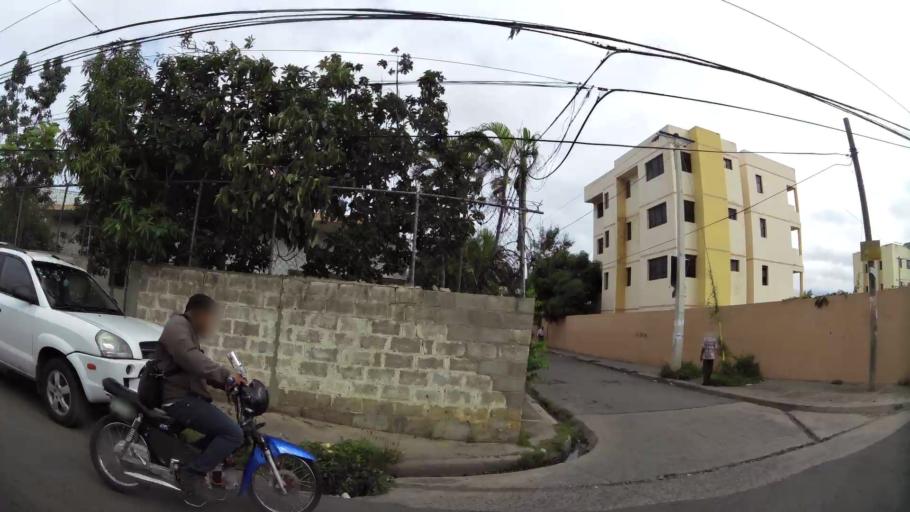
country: DO
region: Santiago
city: Santiago de los Caballeros
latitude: 19.4609
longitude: -70.6696
